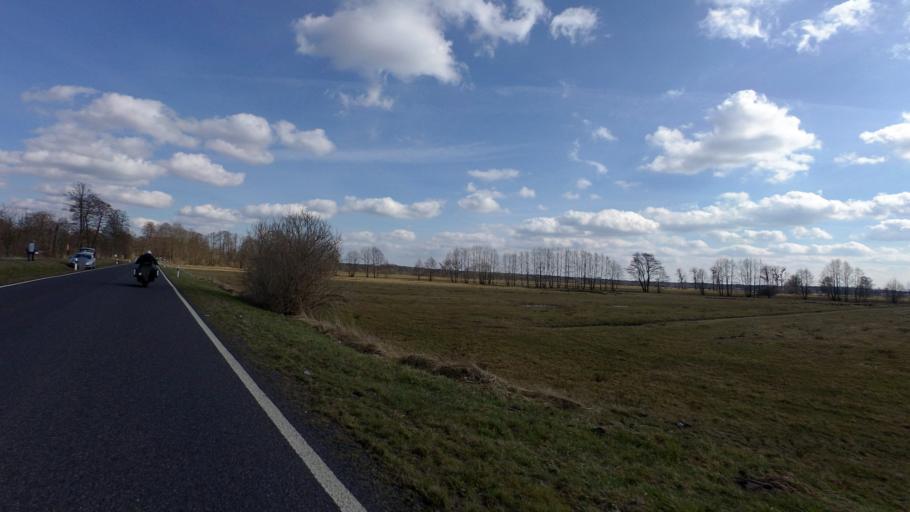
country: DE
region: Brandenburg
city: Marienwerder
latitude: 52.8397
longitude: 13.5614
